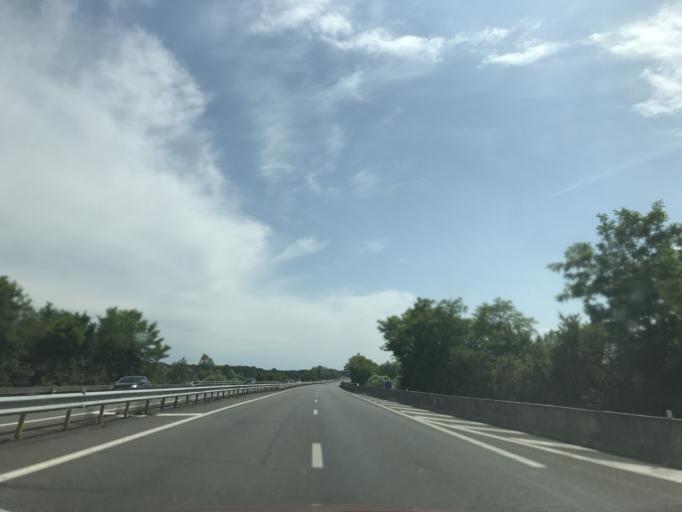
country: FR
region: Centre
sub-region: Departement du Cher
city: Orval
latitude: 46.7847
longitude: 2.4115
